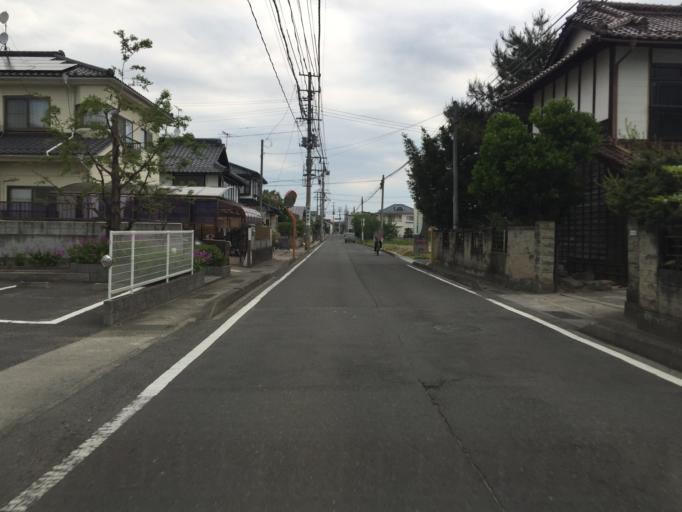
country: JP
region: Fukushima
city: Hobaramachi
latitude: 37.8143
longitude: 140.4975
